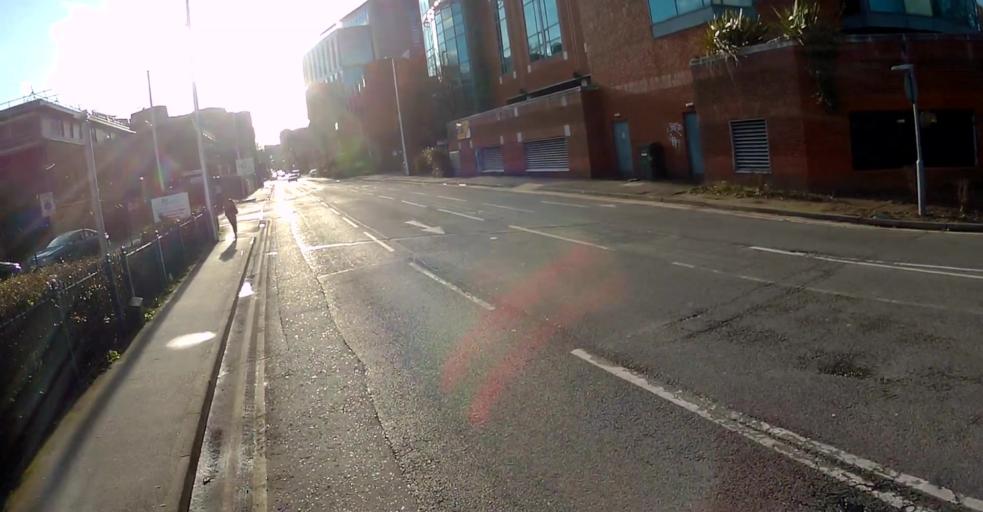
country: GB
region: England
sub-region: Surrey
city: Woking
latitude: 51.3232
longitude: -0.5534
